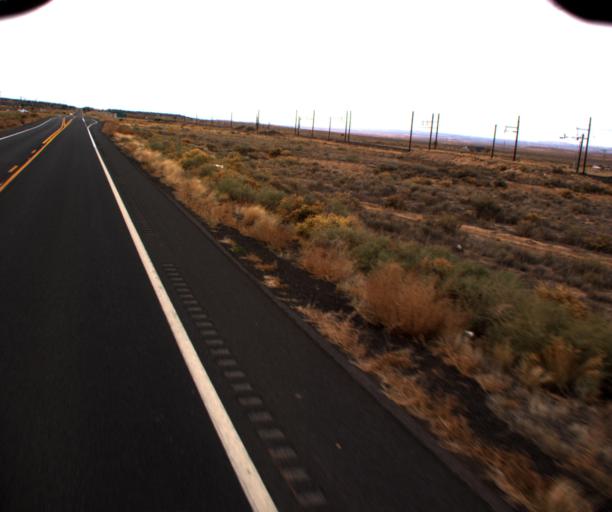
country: US
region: Arizona
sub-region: Coconino County
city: Kaibito
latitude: 36.4625
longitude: -110.6891
